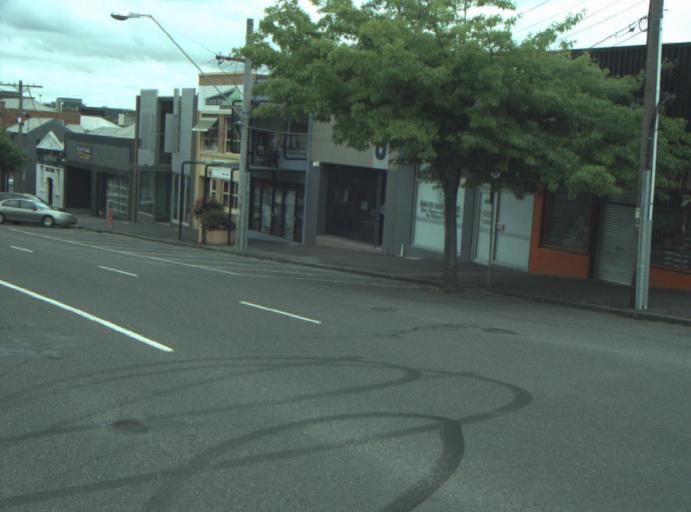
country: AU
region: Victoria
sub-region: Greater Geelong
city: Geelong
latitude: -38.1497
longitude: 144.3568
